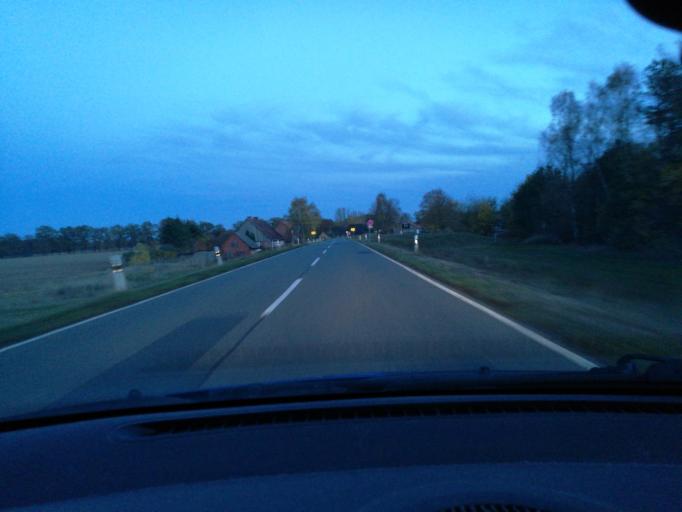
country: DE
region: Lower Saxony
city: Gartow
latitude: 53.0303
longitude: 11.4634
